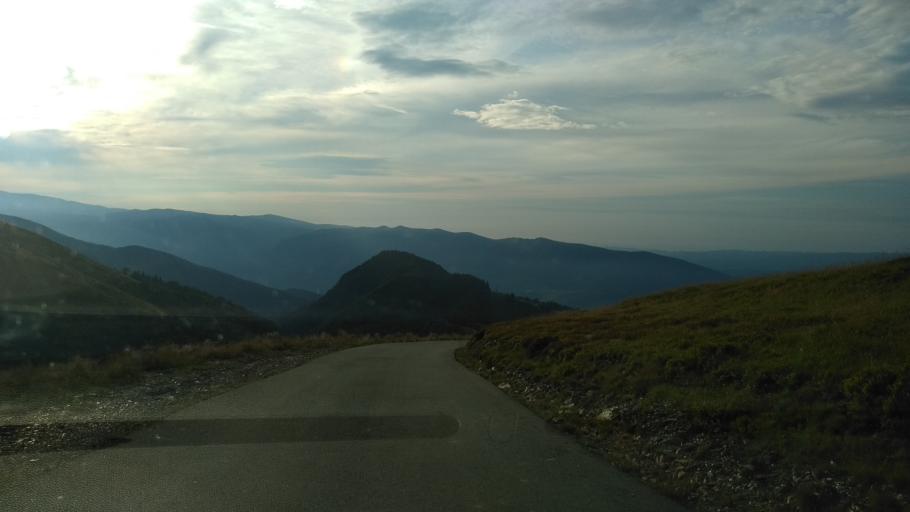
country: RO
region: Hunedoara
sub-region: Municipiul  Vulcan
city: Jiu-Paroseni
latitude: 45.3118
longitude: 23.3069
